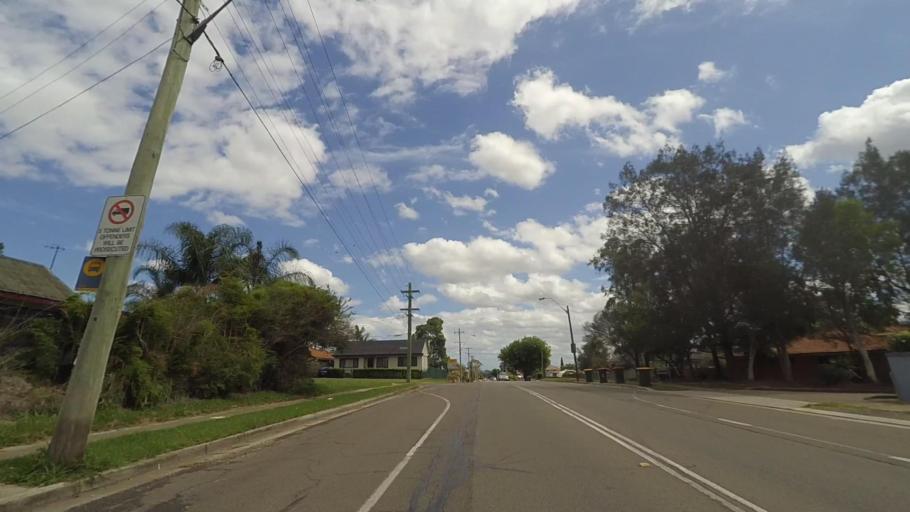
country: AU
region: New South Wales
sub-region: Holroyd
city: Guildford West
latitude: -33.8455
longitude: 150.9625
